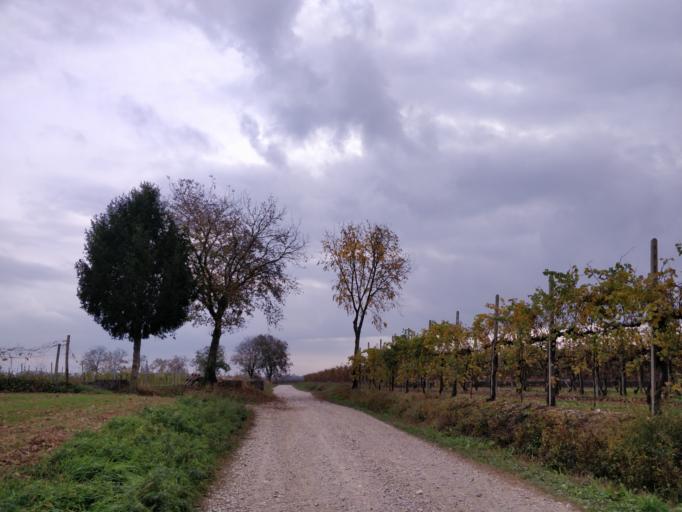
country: IT
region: Friuli Venezia Giulia
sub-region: Provincia di Udine
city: Bertiolo
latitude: 45.9385
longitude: 13.0564
